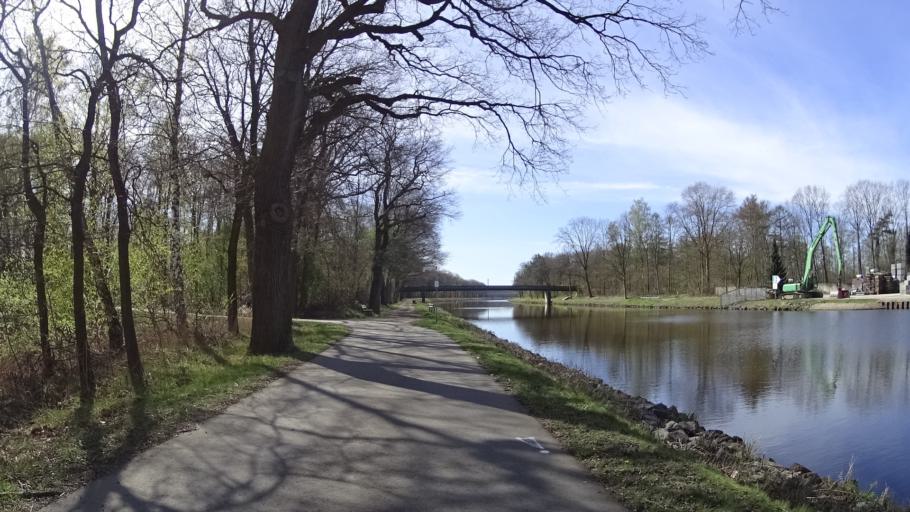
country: DE
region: Lower Saxony
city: Geeste
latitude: 52.5791
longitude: 7.3115
